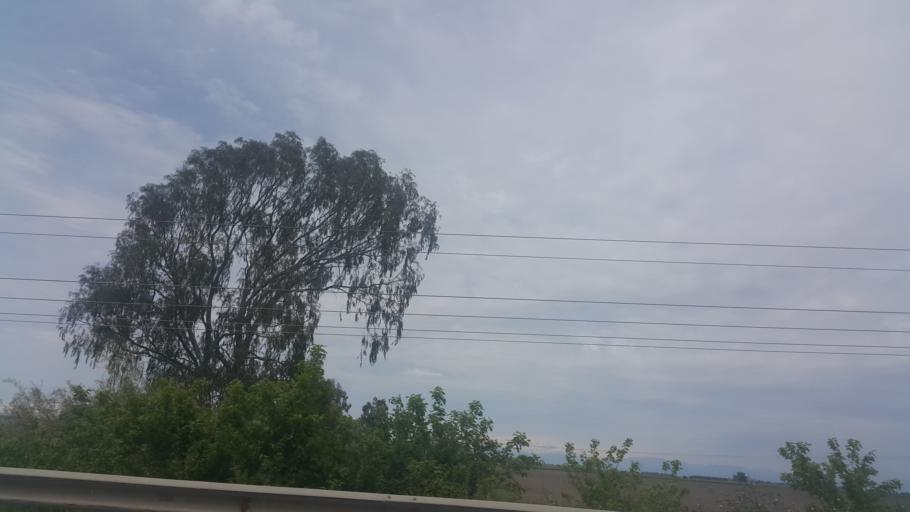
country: TR
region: Adana
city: Ceyhan
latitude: 37.0300
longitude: 35.7383
